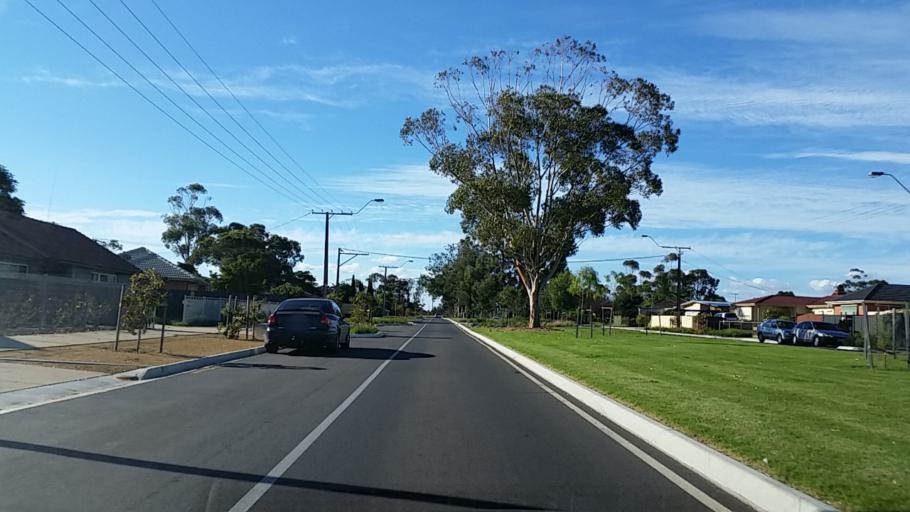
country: AU
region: South Australia
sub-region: Playford
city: Smithfield
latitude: -34.6836
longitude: 138.6715
